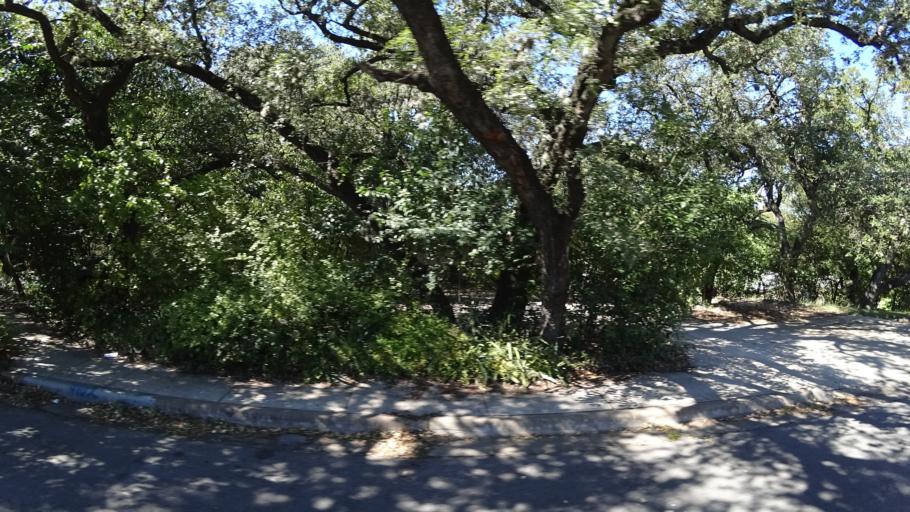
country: US
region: Texas
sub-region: Travis County
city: Austin
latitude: 30.3128
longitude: -97.7478
